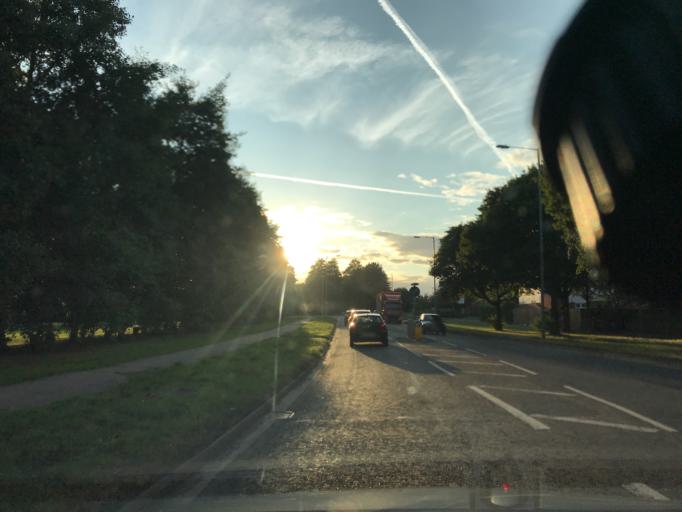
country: GB
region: England
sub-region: Buckinghamshire
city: Aylesbury
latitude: 51.8217
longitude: -0.7921
